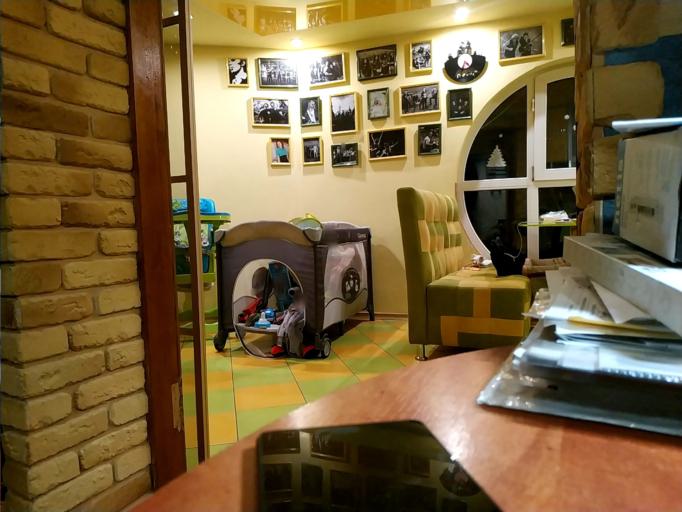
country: RU
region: Orjol
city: Naryshkino
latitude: 53.0565
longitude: 35.6758
